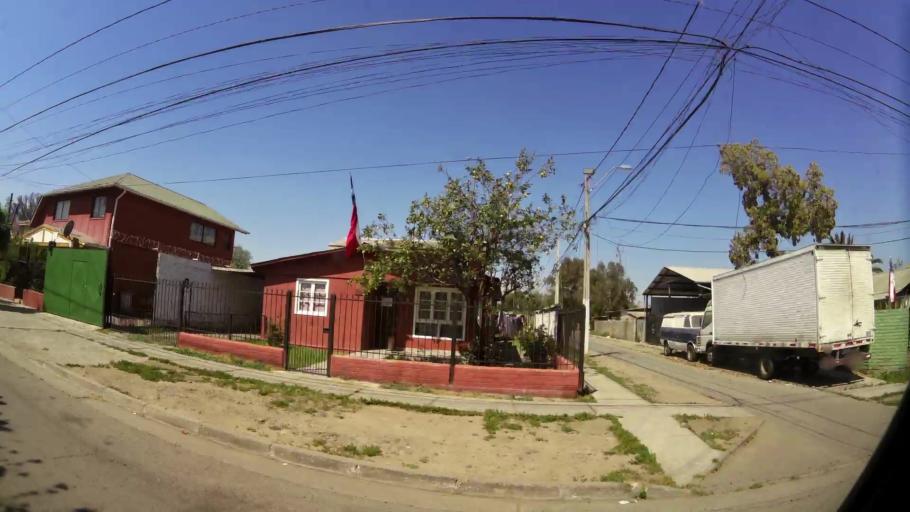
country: CL
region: Santiago Metropolitan
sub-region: Provincia de Talagante
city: Penaflor
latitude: -33.5723
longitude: -70.8111
